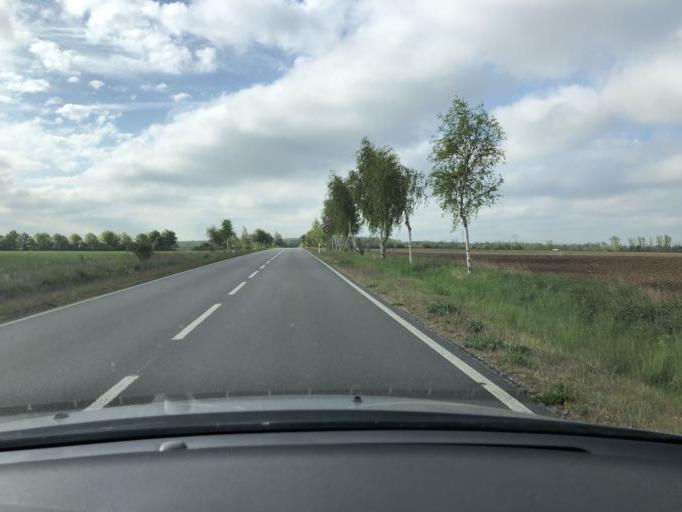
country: DE
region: Saxony
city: Neukieritzsch
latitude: 51.1619
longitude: 12.4193
